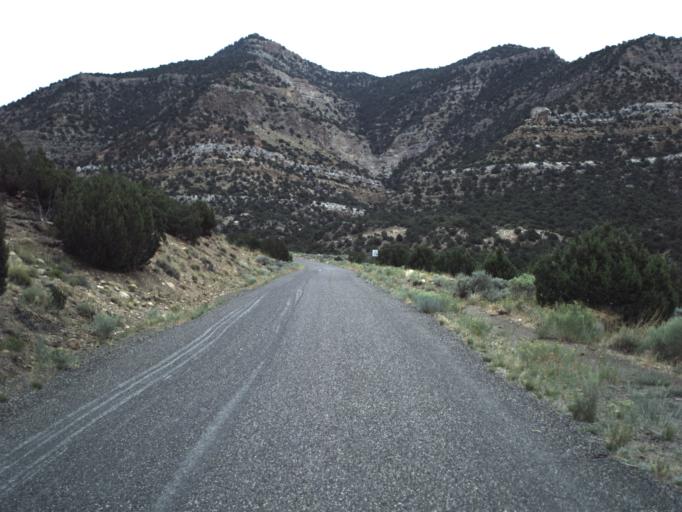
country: US
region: Utah
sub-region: Carbon County
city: East Carbon City
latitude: 39.4525
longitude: -110.3691
